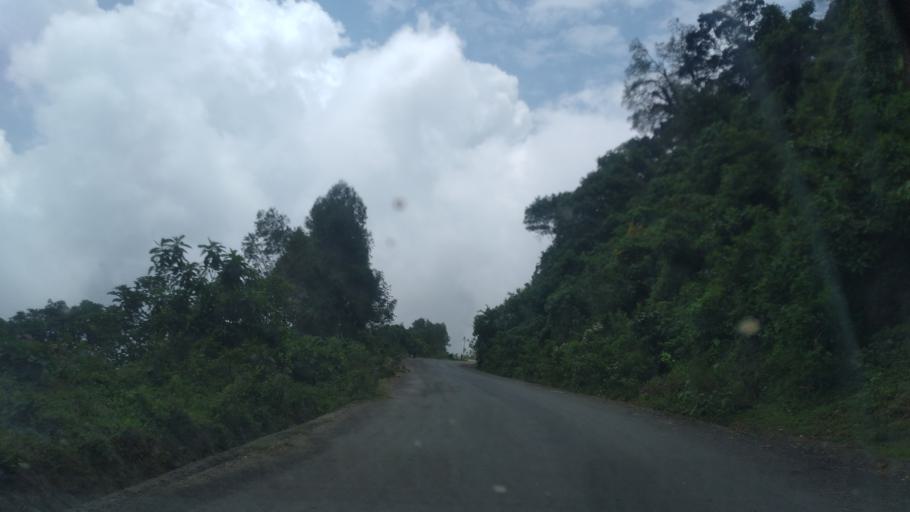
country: ET
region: Southern Nations, Nationalities, and People's Region
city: Bonga
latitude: 7.1144
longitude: 36.7237
